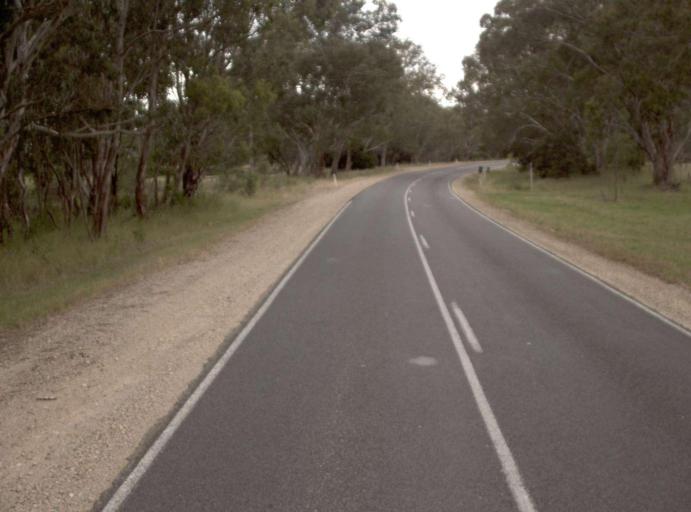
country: AU
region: Victoria
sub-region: Wellington
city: Sale
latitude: -38.1784
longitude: 147.1463
